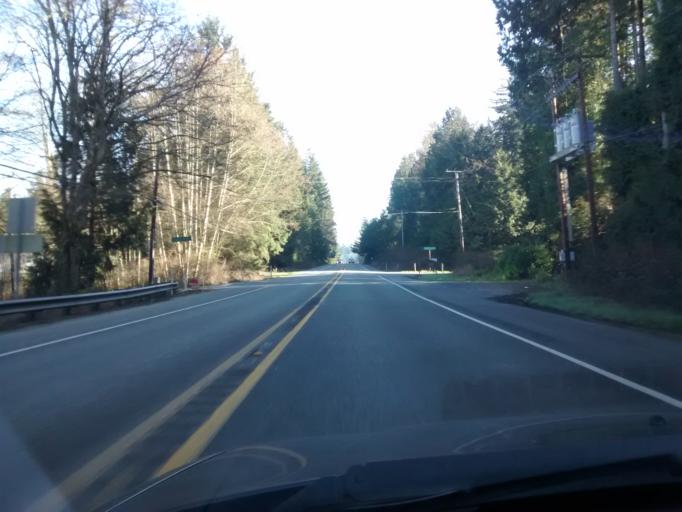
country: US
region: Washington
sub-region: Kitsap County
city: Lofall
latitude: 47.8262
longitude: -122.6339
